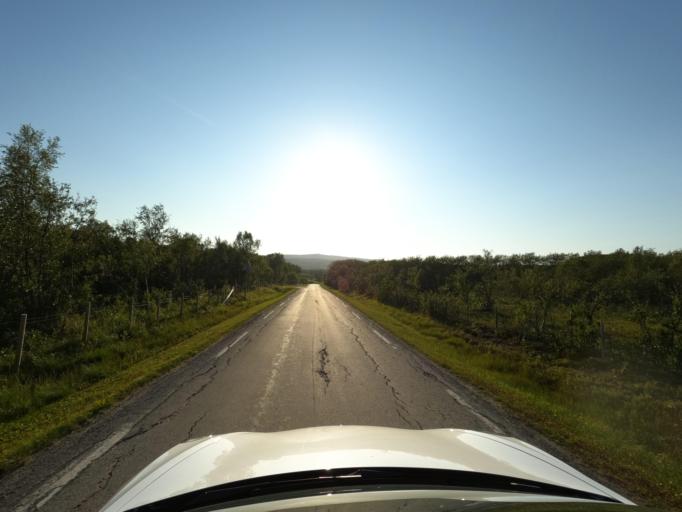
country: NO
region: Troms
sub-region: Skanland
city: Evenskjer
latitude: 68.4634
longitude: 16.6715
